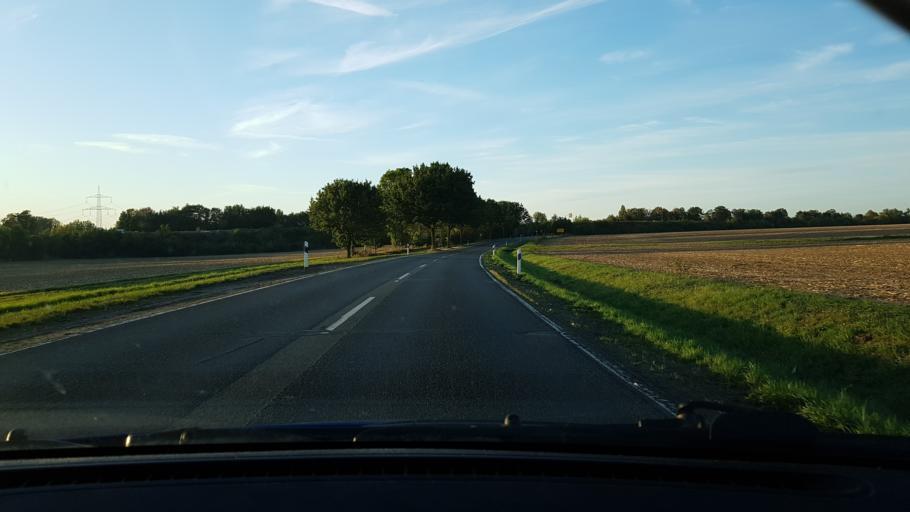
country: DE
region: Lower Saxony
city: Lauenau
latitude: 52.2862
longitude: 9.3614
